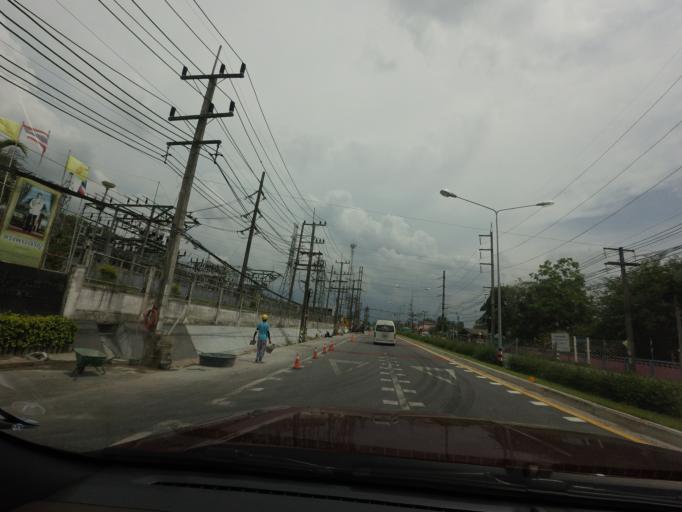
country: TH
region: Yala
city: Yala
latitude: 6.4996
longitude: 101.2674
